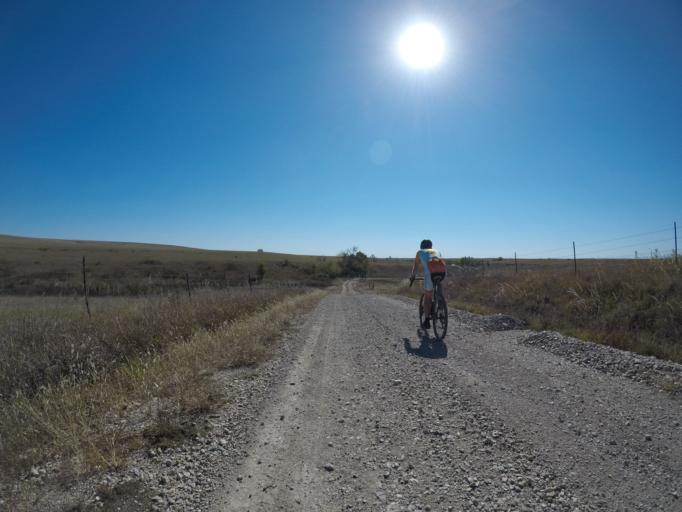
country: US
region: Kansas
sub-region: Wabaunsee County
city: Alma
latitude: 39.0236
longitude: -96.4093
